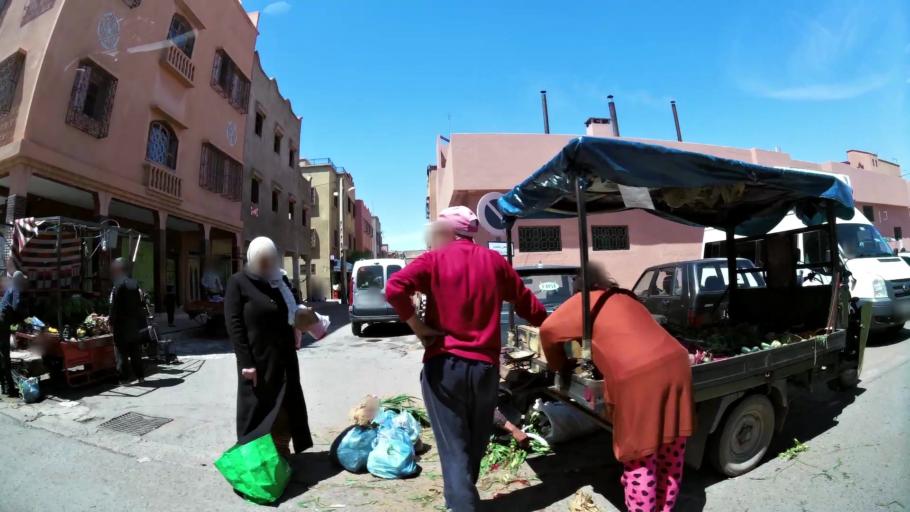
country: MA
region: Marrakech-Tensift-Al Haouz
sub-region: Marrakech
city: Marrakesh
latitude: 31.6370
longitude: -8.0597
